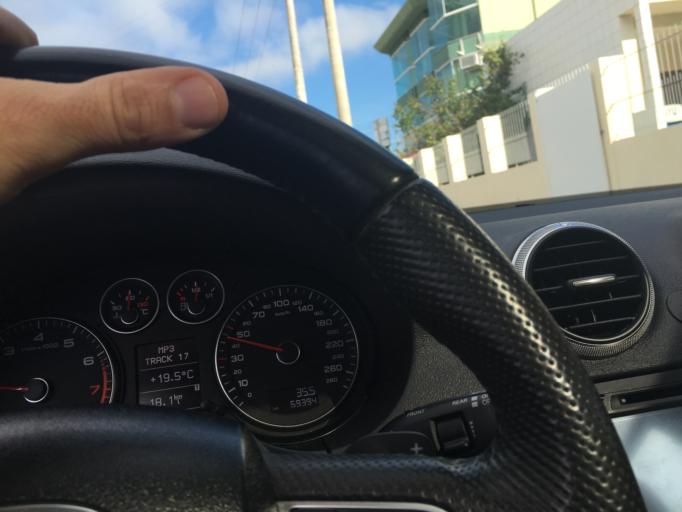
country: BR
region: Santa Catarina
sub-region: Florianopolis
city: Itacorubi
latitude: -27.4375
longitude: -48.4075
